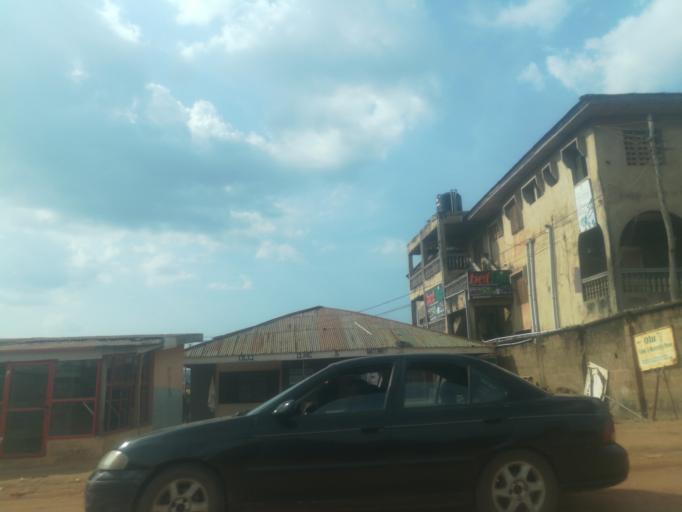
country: NG
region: Ogun
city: Abeokuta
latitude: 7.1165
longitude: 3.3166
